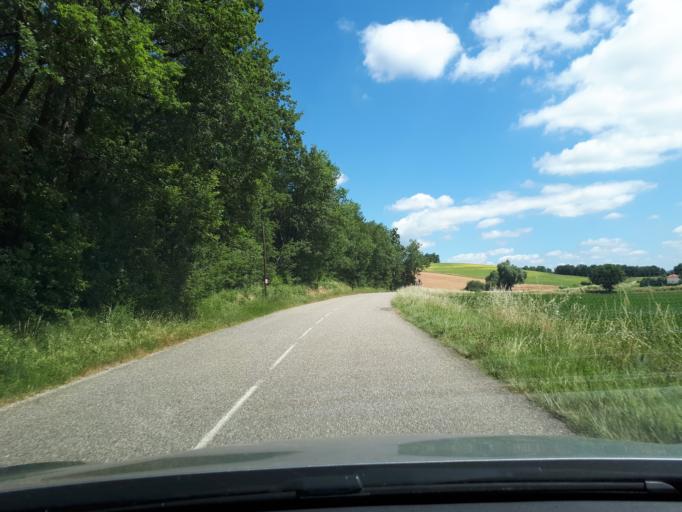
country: FR
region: Midi-Pyrenees
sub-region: Departement du Tarn-et-Garonne
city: Auvillar
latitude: 44.0098
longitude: 0.8196
